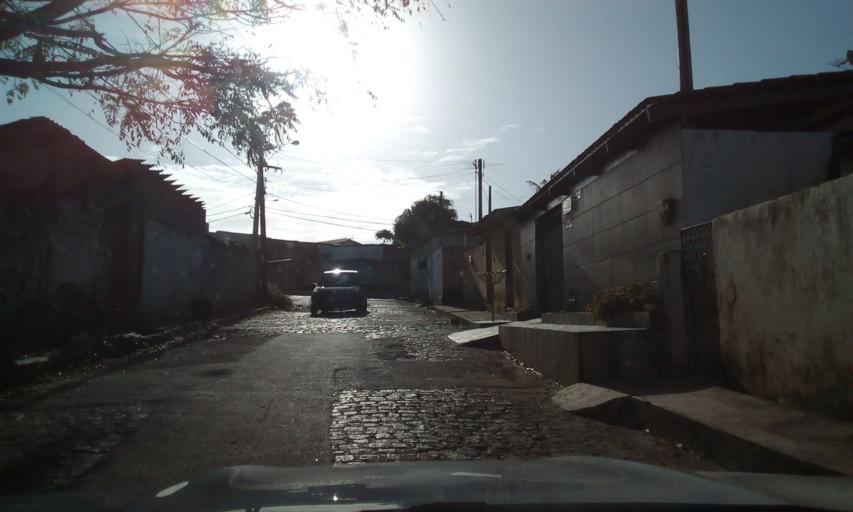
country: BR
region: Paraiba
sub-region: Joao Pessoa
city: Joao Pessoa
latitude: -7.1531
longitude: -34.8447
